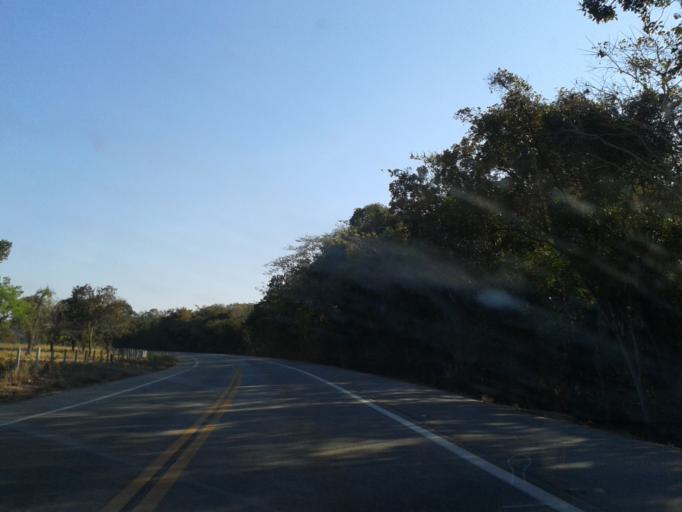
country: BR
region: Goias
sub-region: Itapirapua
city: Itapirapua
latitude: -15.3079
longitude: -50.4434
